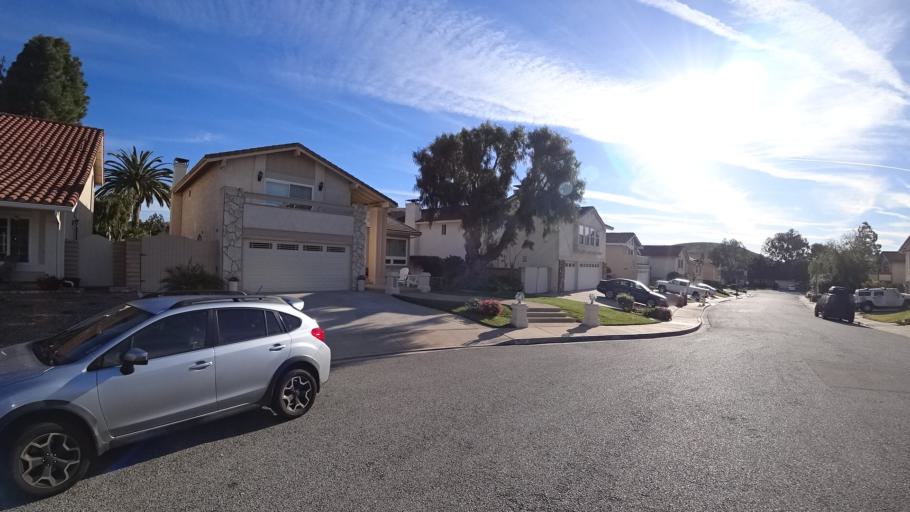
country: US
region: California
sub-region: Ventura County
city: Casa Conejo
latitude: 34.1903
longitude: -118.9589
